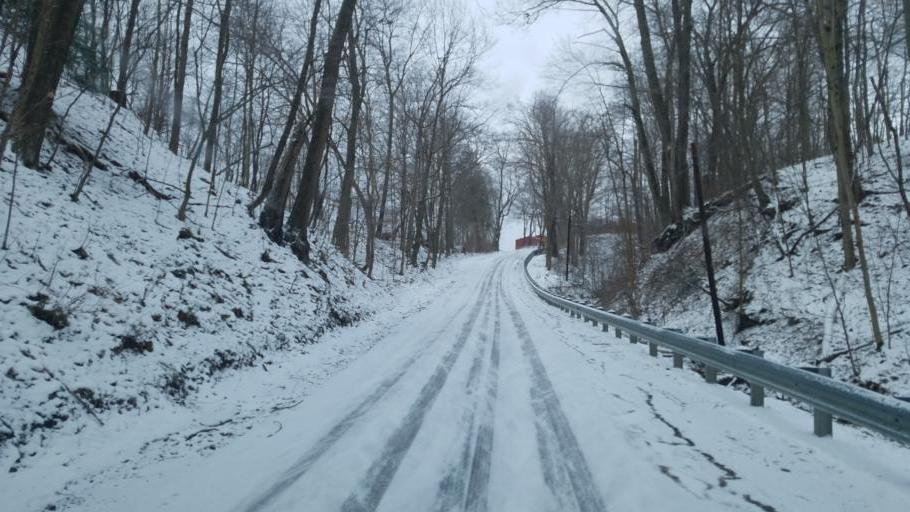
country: US
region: Pennsylvania
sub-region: Crawford County
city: Cochranton
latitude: 41.4701
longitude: -80.0193
